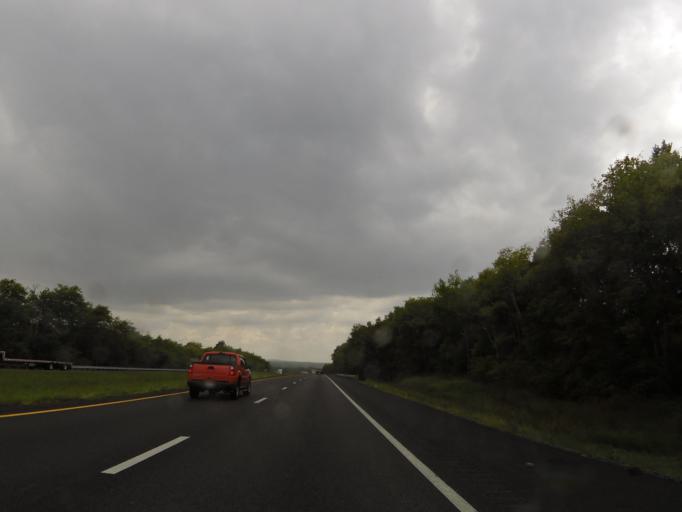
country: US
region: Tennessee
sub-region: Wilson County
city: Lebanon
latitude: 36.1936
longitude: -86.1963
